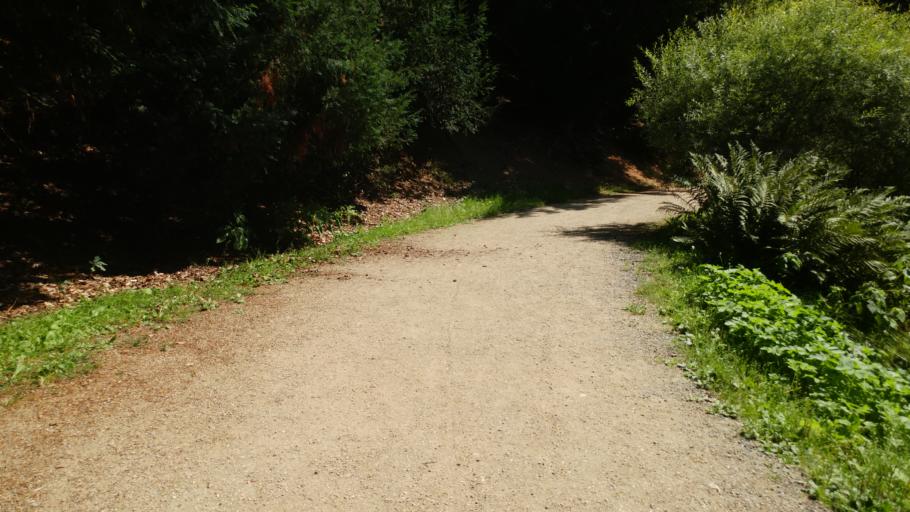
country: CZ
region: Central Bohemia
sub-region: Okres Praha-Zapad
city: Pruhonice
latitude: 49.9965
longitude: 14.5633
